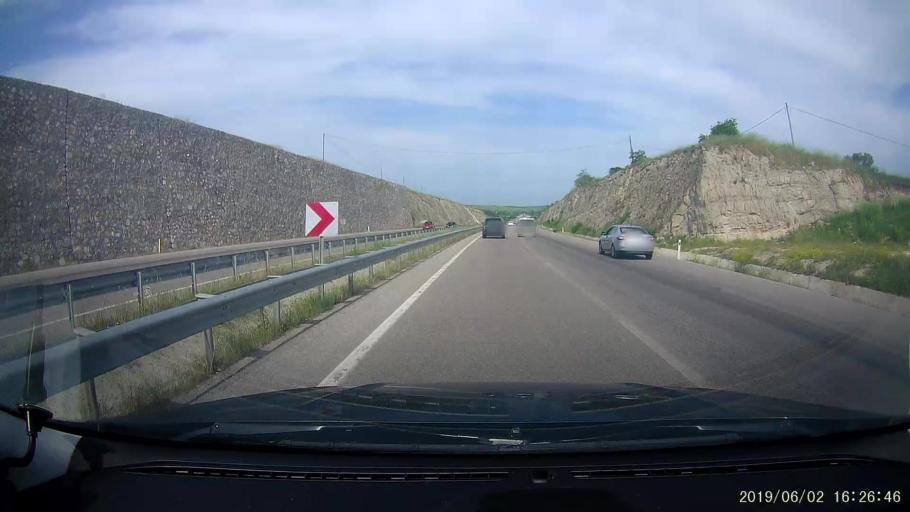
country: TR
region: Samsun
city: Ladik
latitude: 41.0013
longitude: 35.8106
